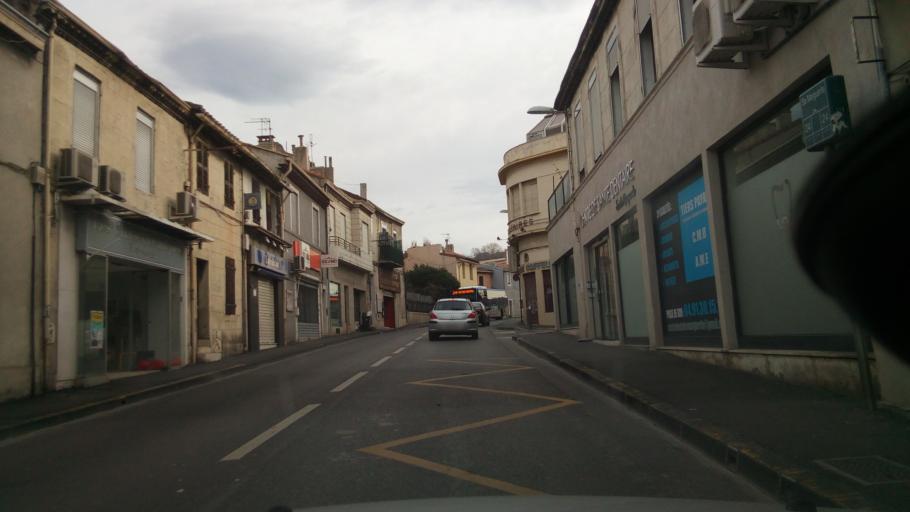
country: FR
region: Provence-Alpes-Cote d'Azur
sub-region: Departement des Bouches-du-Rhone
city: Marseille 09
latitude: 43.2682
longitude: 5.4064
